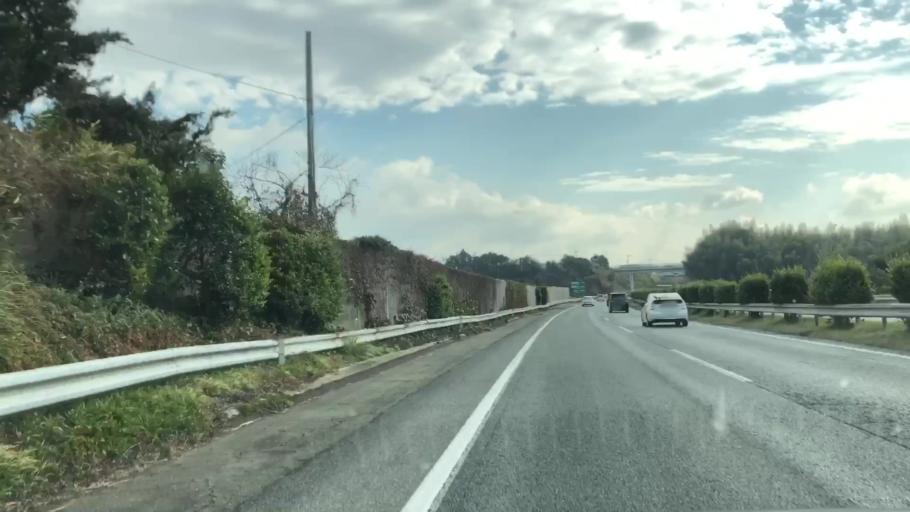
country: JP
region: Fukuoka
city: Setakamachi-takayanagi
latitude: 33.1364
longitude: 130.5156
